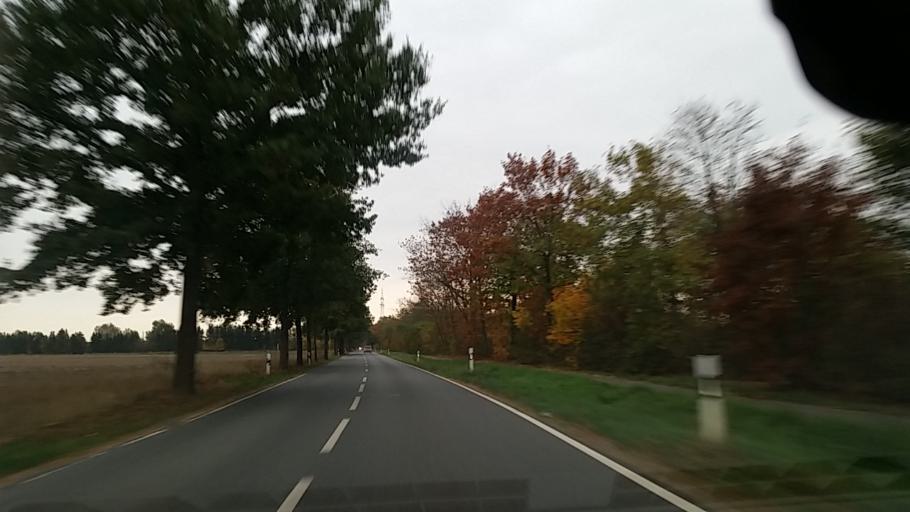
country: DE
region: Lower Saxony
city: Jembke
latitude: 52.4698
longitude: 10.7744
